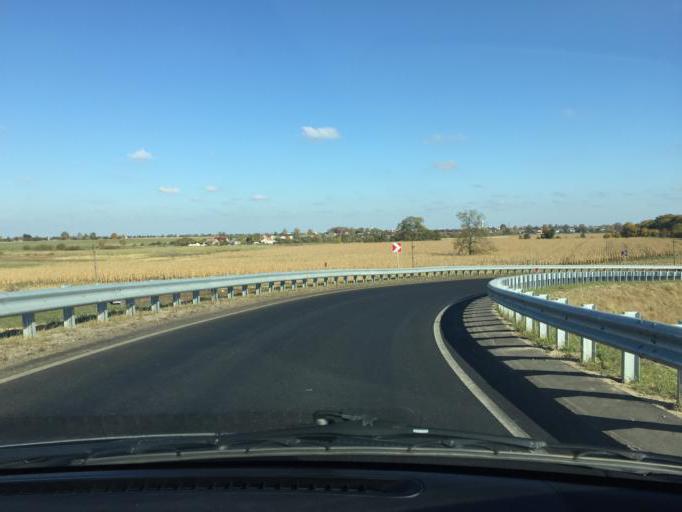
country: BY
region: Minsk
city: Slutsk
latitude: 53.0109
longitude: 27.4871
